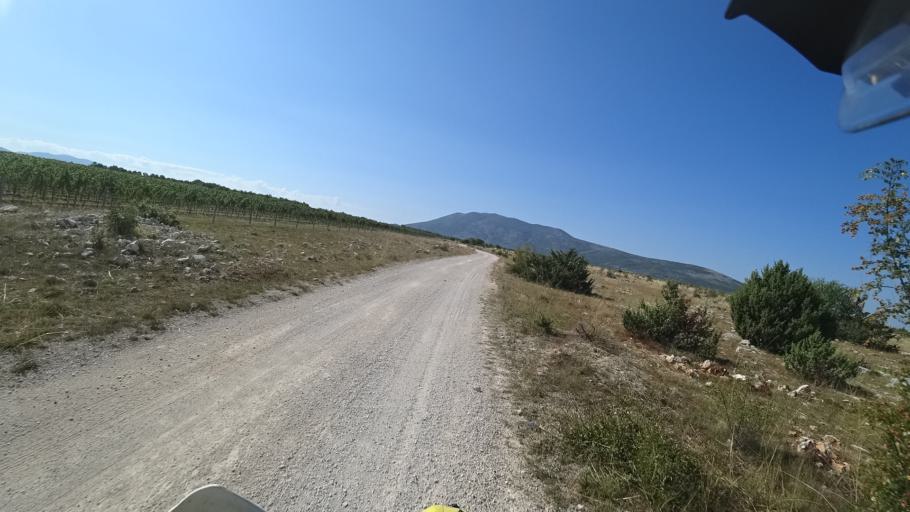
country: HR
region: Sibensko-Kniniska
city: Knin
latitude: 43.9913
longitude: 16.1927
